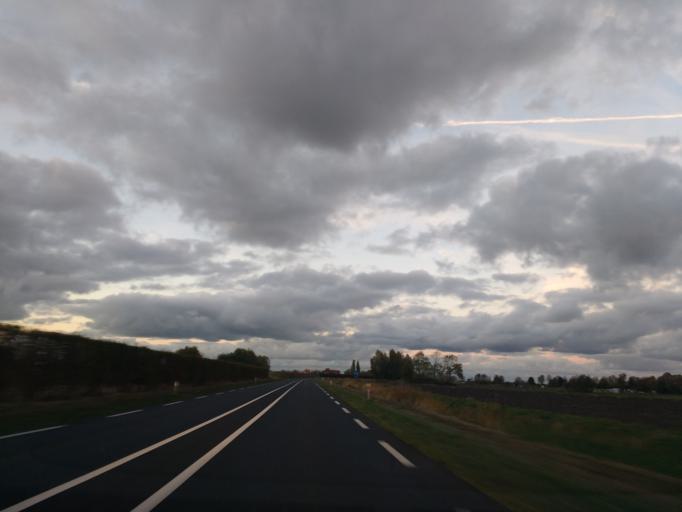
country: NL
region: Zeeland
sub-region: Gemeente Sluis
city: Sluis
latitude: 51.3263
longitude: 3.4755
